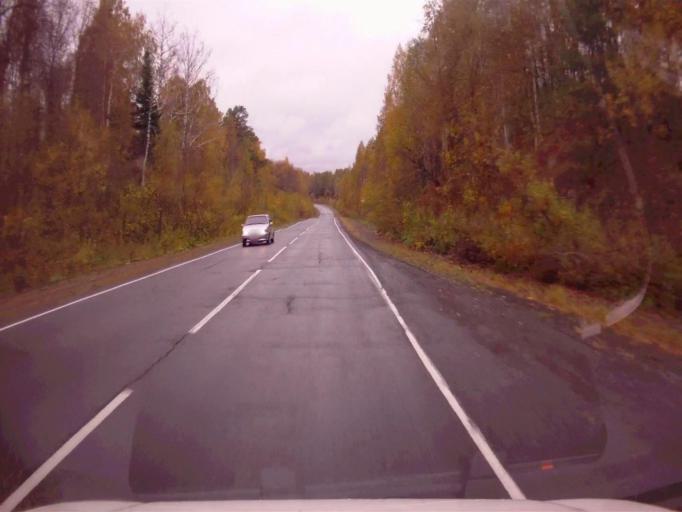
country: RU
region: Chelyabinsk
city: Nizhniy Ufaley
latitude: 56.0676
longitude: 60.0148
